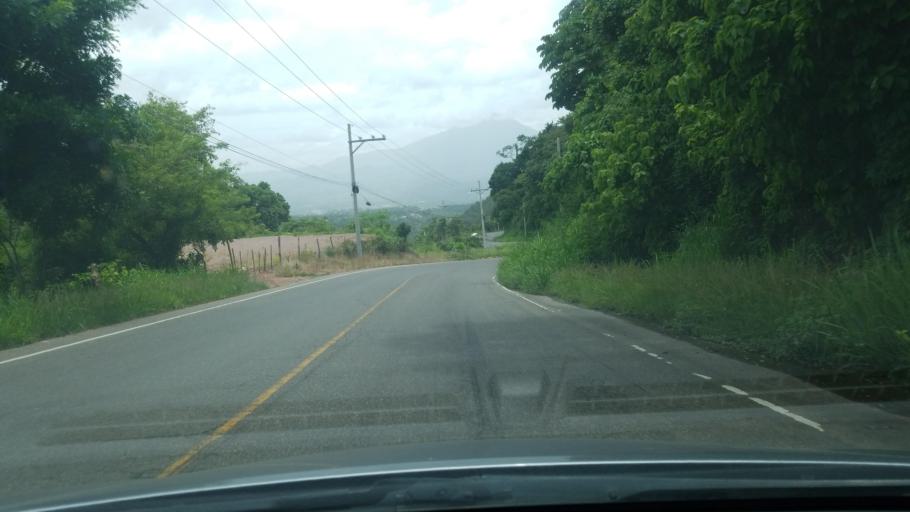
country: HN
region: Copan
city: Ojos de Agua
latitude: 14.6744
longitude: -88.8239
